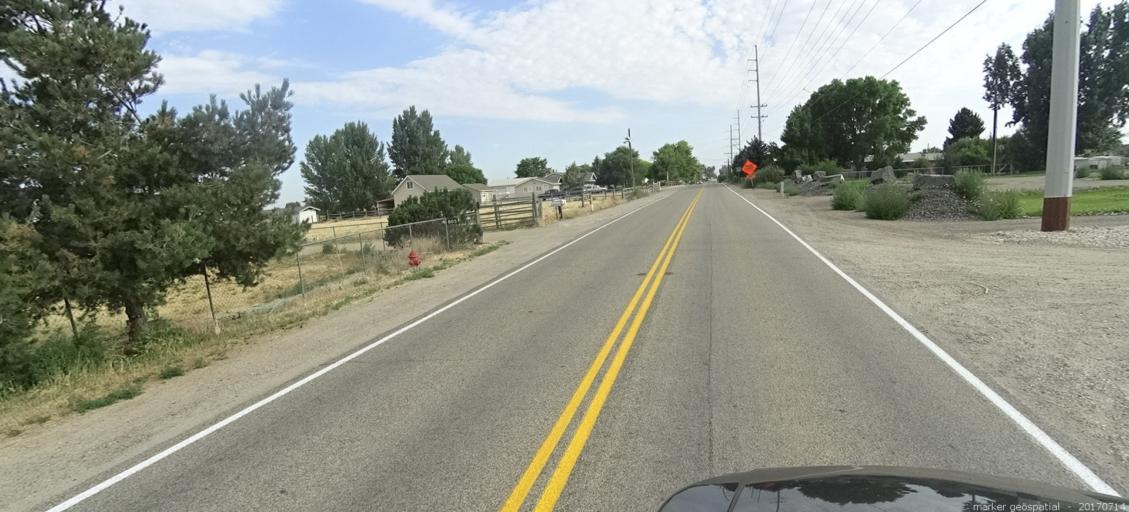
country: US
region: Idaho
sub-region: Ada County
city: Kuna
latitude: 43.4832
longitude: -116.4137
